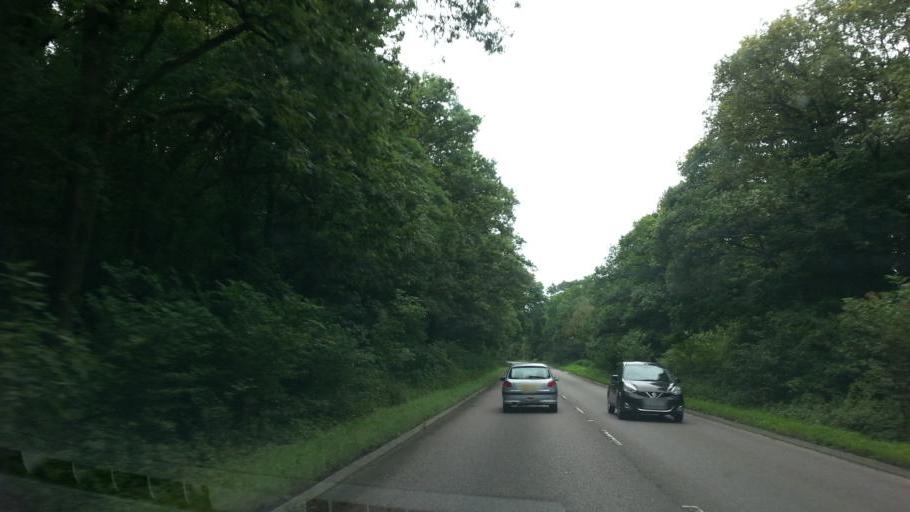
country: GB
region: England
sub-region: Wiltshire
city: Trowbridge
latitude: 51.3185
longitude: -2.1641
